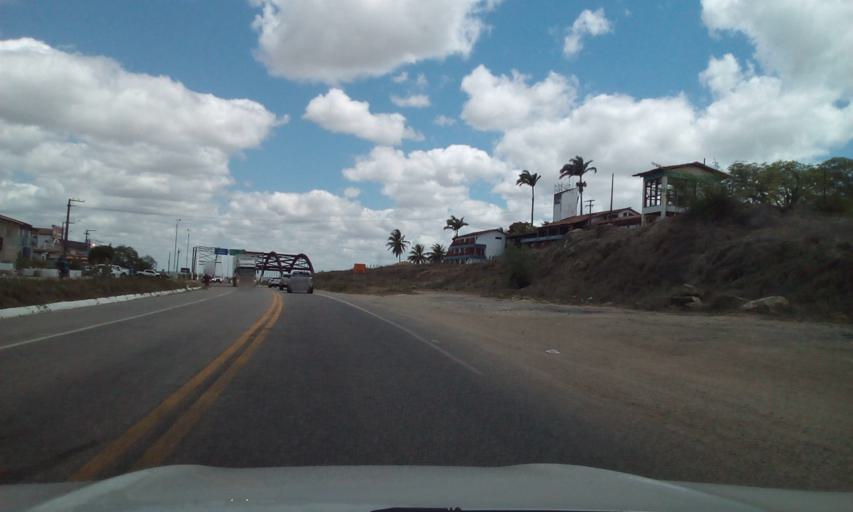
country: BR
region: Sergipe
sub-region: Propria
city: Propria
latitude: -10.2160
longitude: -36.8233
